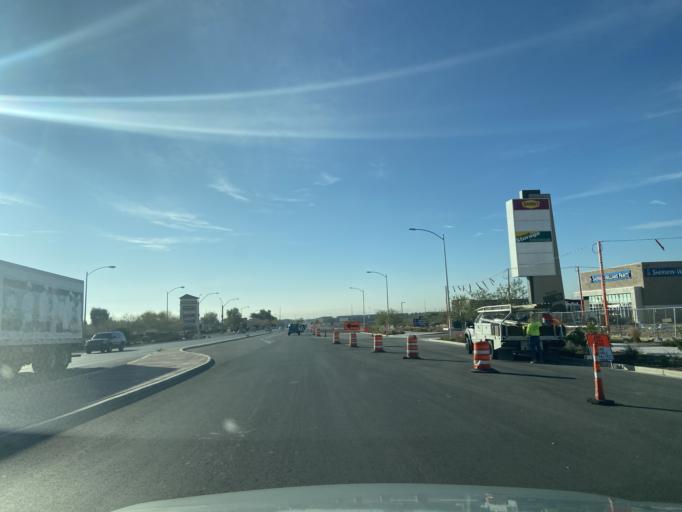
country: US
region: Nevada
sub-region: Clark County
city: Nellis Air Force Base
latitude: 36.2852
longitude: -115.1350
